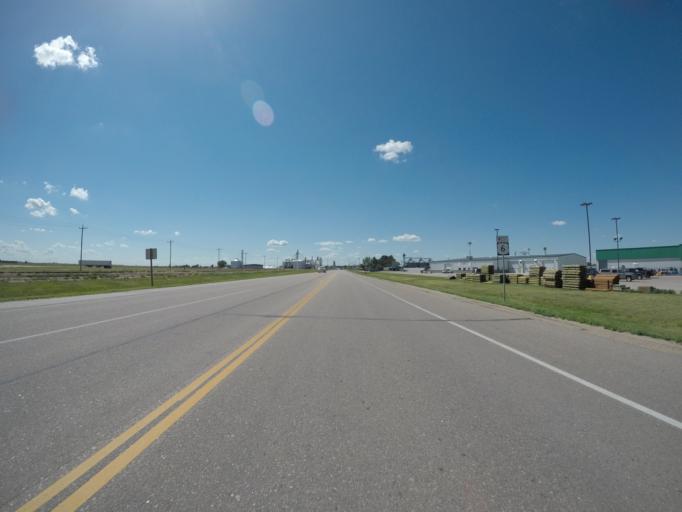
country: US
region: Nebraska
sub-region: Chase County
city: Imperial
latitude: 40.5075
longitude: -101.6293
